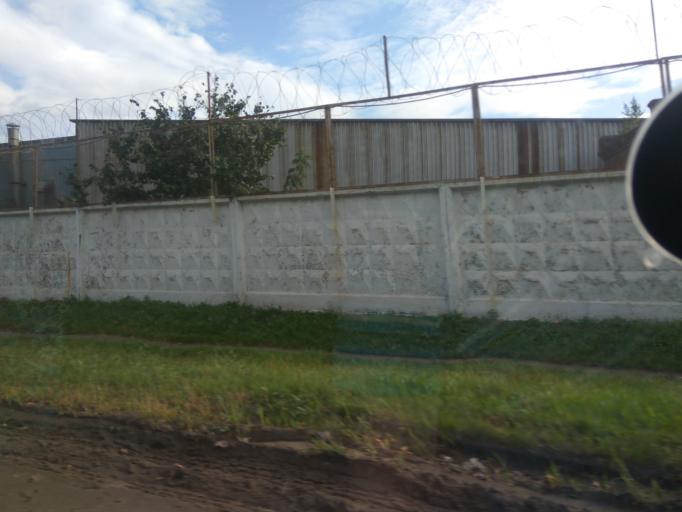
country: RU
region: Moskovskaya
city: Ramenskoye
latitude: 55.5672
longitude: 38.2660
